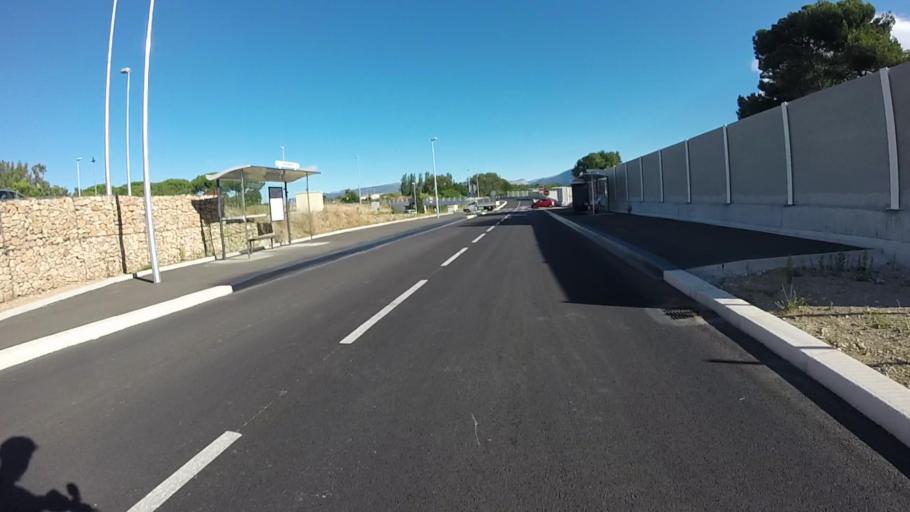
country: FR
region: Provence-Alpes-Cote d'Azur
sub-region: Departement des Alpes-Maritimes
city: Biot
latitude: 43.6041
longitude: 7.0832
